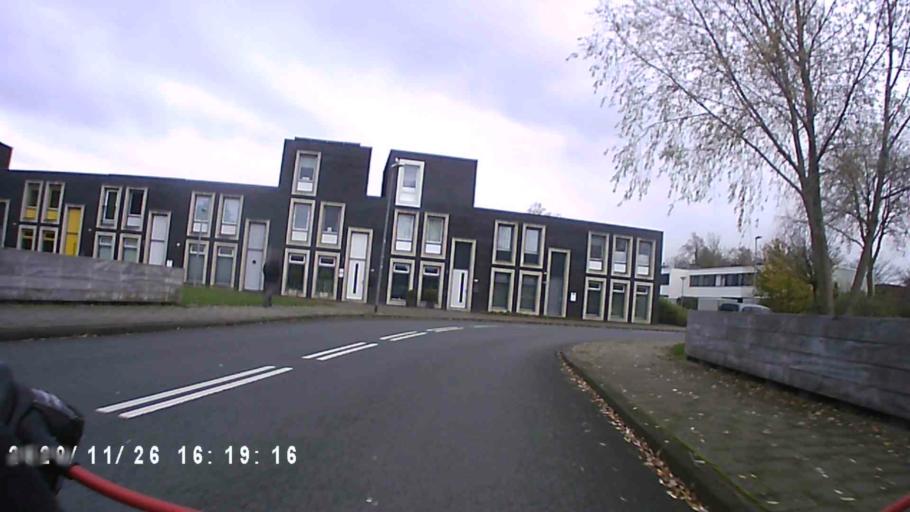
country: NL
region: Groningen
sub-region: Gemeente Groningen
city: Oosterpark
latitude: 53.2369
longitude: 6.6252
